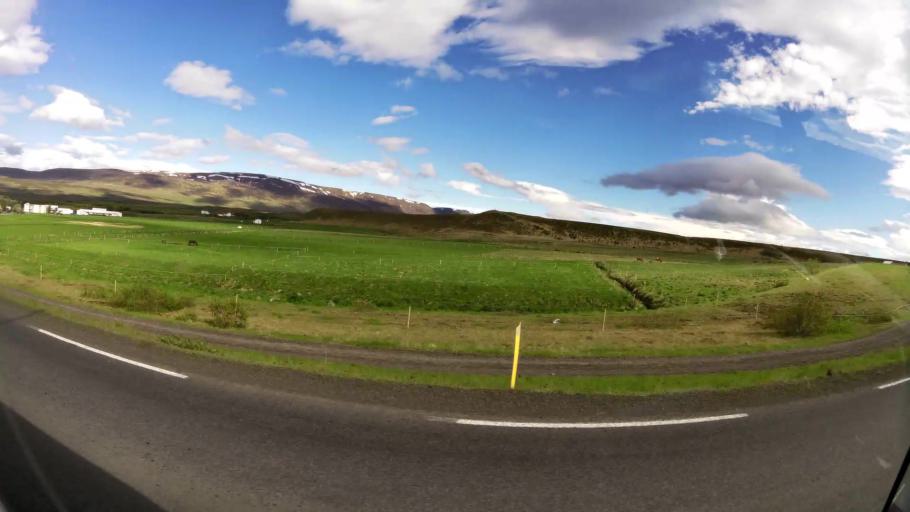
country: IS
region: Northwest
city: Saudarkrokur
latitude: 65.6543
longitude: -20.2866
